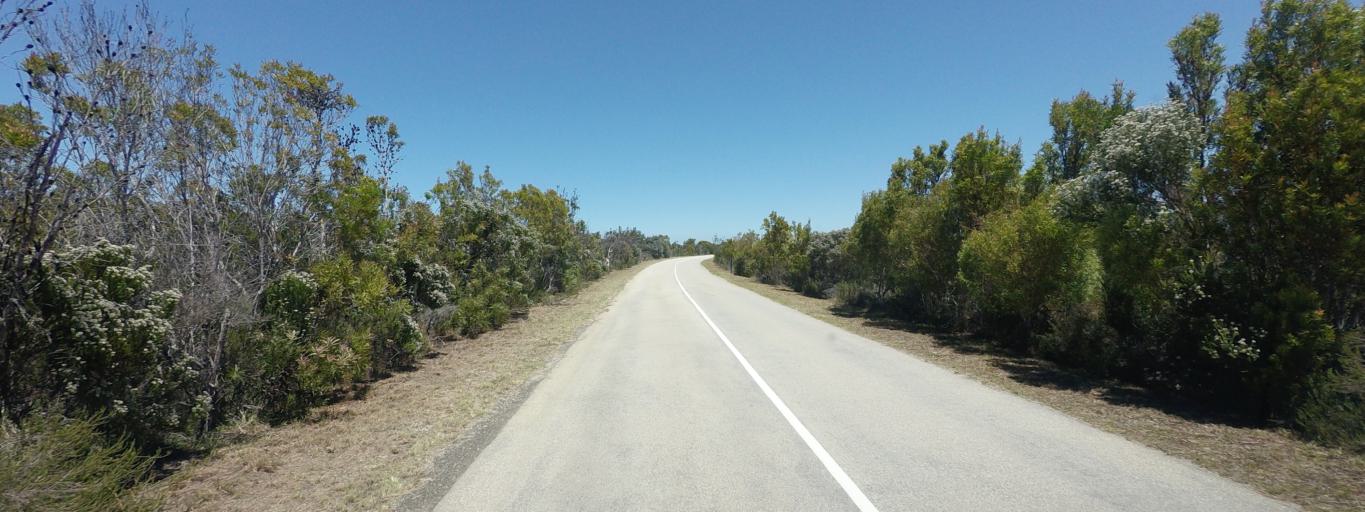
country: ZA
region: Western Cape
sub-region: Eden District Municipality
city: Plettenberg Bay
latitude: -33.9605
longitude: 23.5327
